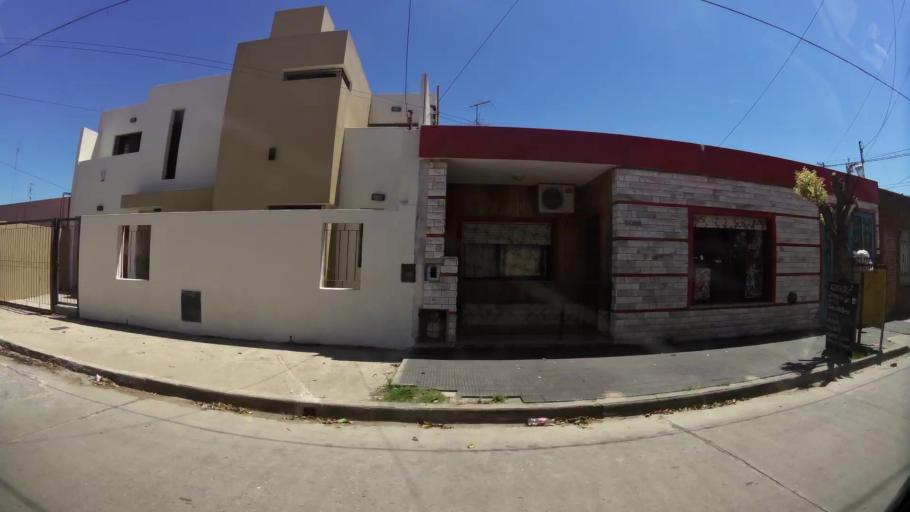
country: AR
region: Cordoba
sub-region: Departamento de Capital
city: Cordoba
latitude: -31.4286
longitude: -64.1207
